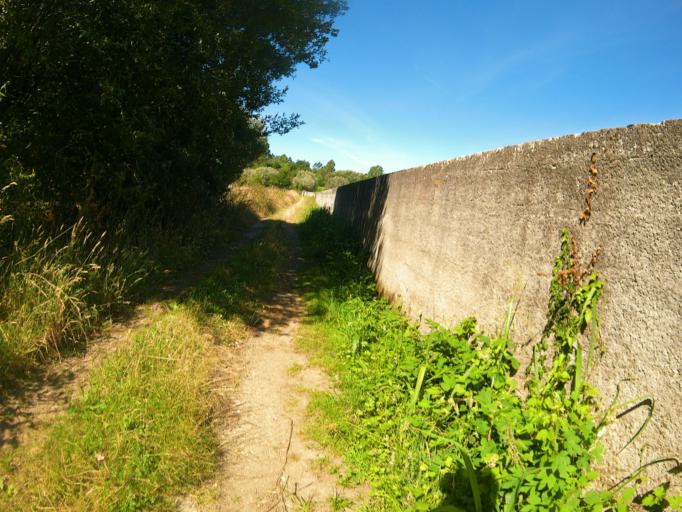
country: PT
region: Viana do Castelo
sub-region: Viana do Castelo
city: Darque
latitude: 41.7187
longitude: -8.6802
